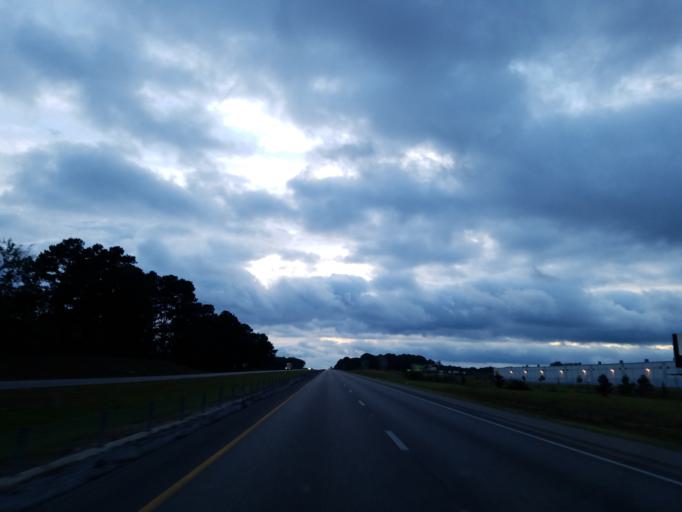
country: US
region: Mississippi
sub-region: Lauderdale County
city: Marion
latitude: 32.3856
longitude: -88.6245
